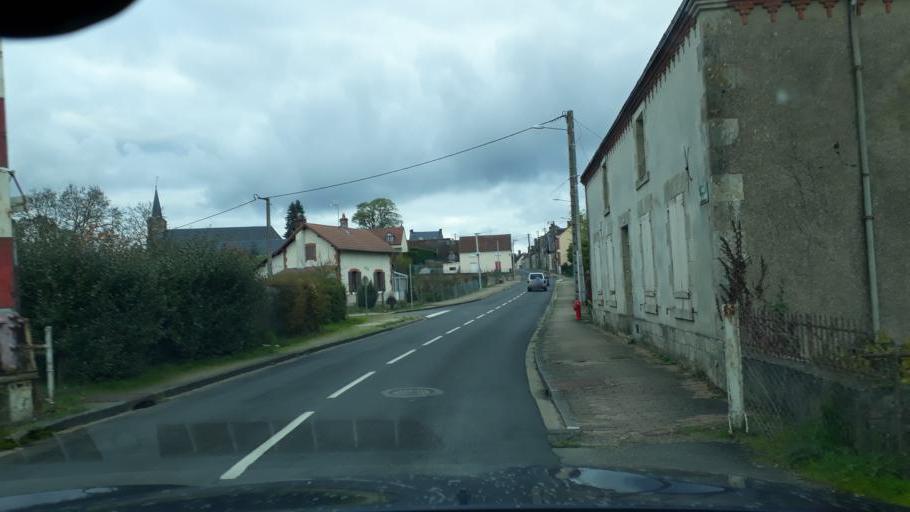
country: FR
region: Centre
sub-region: Departement du Loiret
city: Bray-en-Val
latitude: 47.8102
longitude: 2.3999
